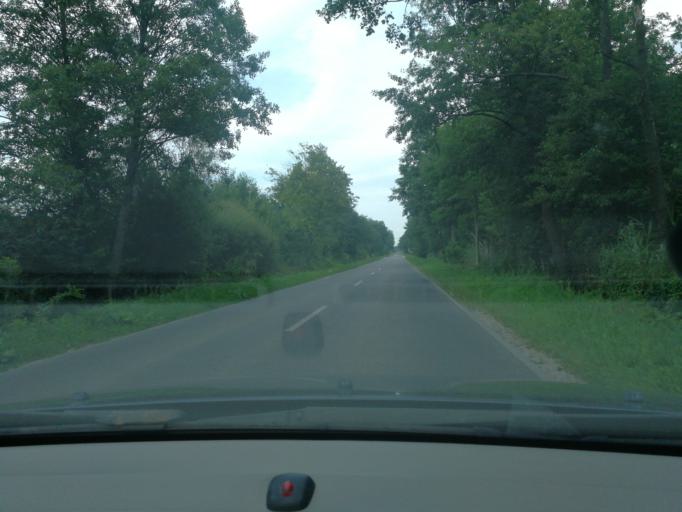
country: PL
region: Masovian Voivodeship
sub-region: Powiat grodziski
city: Grodzisk Mazowiecki
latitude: 52.1365
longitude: 20.6199
